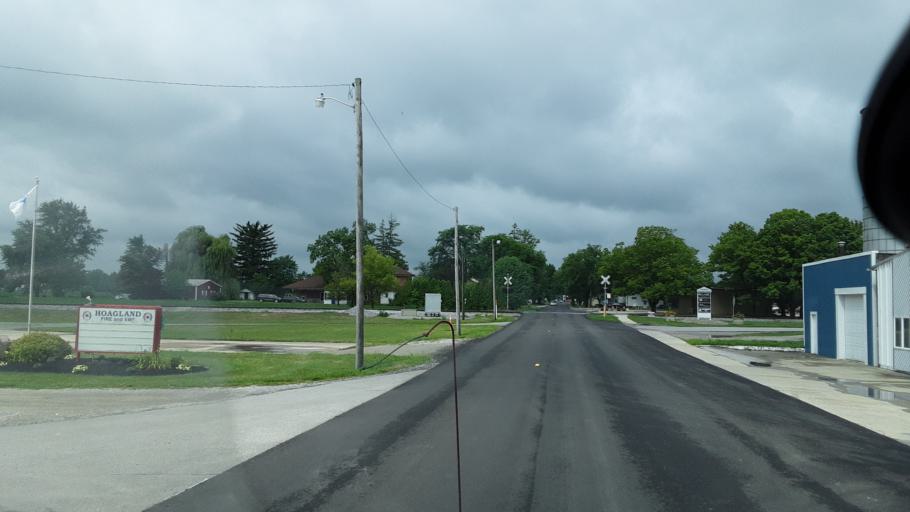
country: US
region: Indiana
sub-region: Allen County
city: New Haven
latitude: 40.9482
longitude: -84.9903
